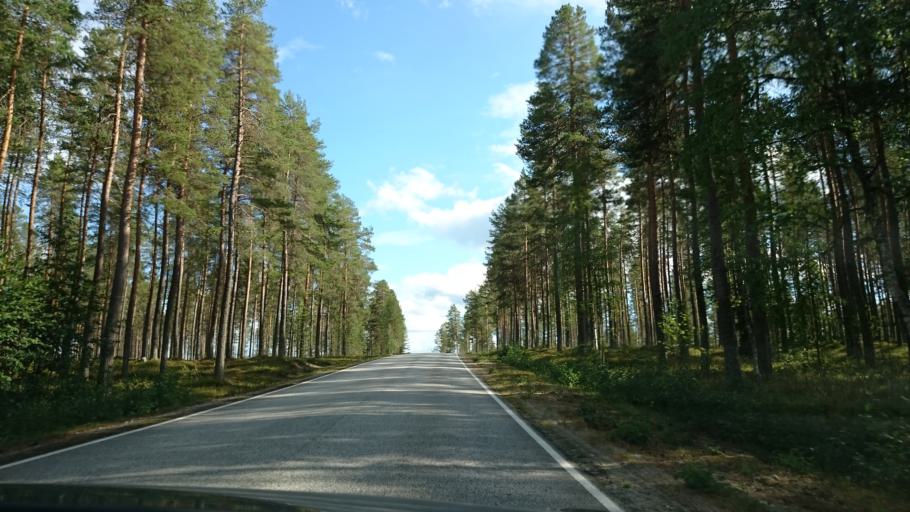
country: FI
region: Kainuu
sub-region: Kehys-Kainuu
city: Suomussalmi
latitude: 64.7678
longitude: 29.3667
